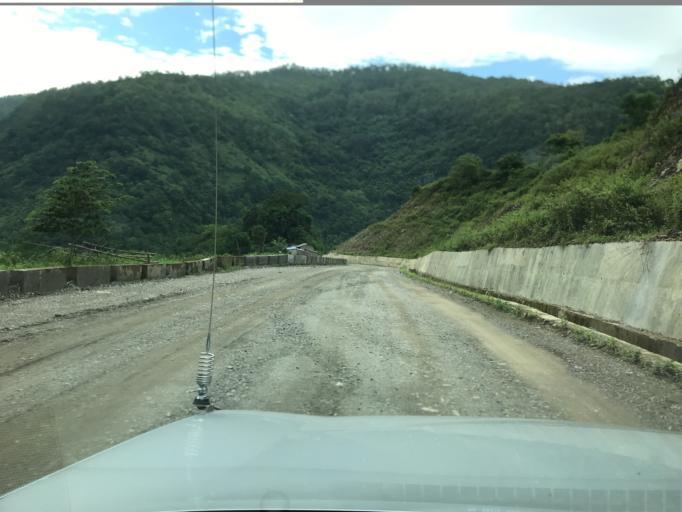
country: TL
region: Dili
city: Dili
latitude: -8.6397
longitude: 125.5095
